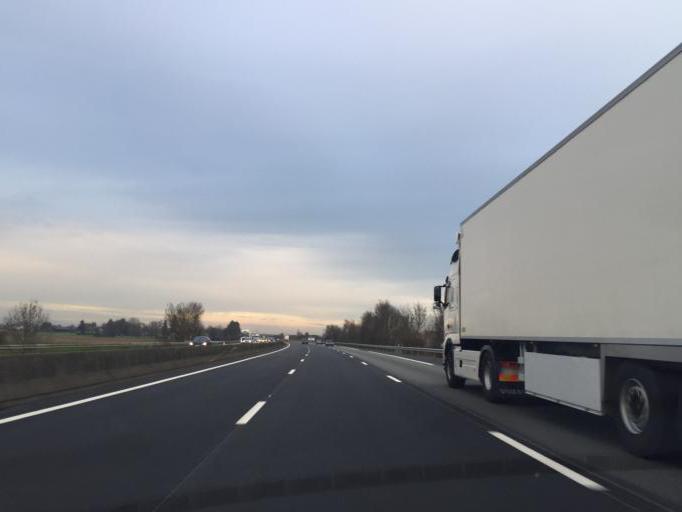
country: FR
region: Rhone-Alpes
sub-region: Departement de l'Ain
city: Guereins
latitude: 46.1141
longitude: 4.7623
